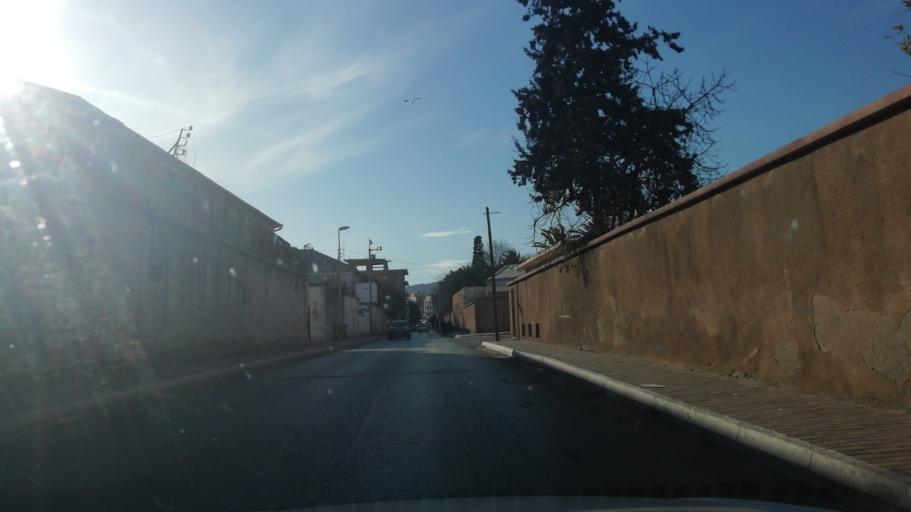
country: DZ
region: Oran
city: Oran
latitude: 35.6933
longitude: -0.6411
